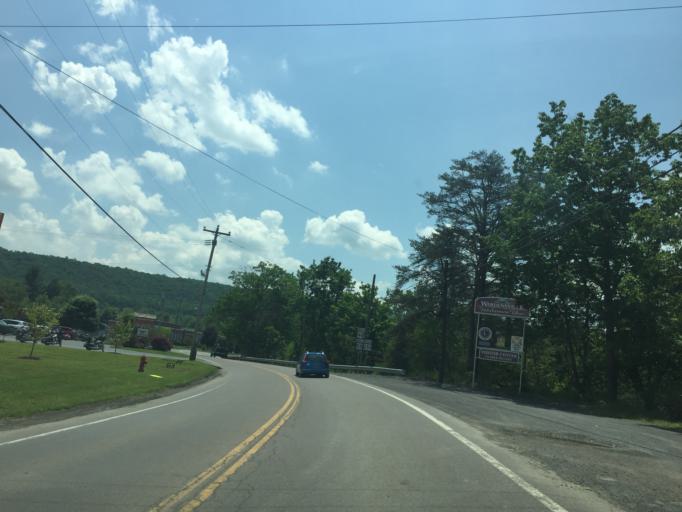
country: US
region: Virginia
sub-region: Shenandoah County
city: Woodstock
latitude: 39.0825
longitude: -78.5920
